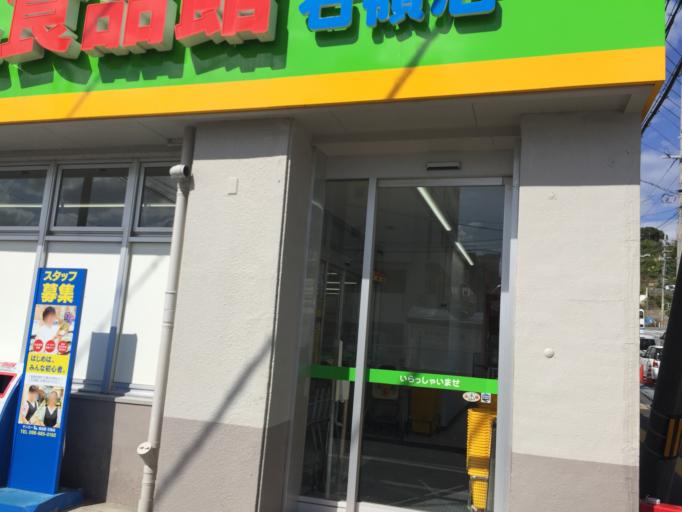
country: JP
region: Okinawa
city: Ginowan
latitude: 26.2334
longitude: 127.7286
